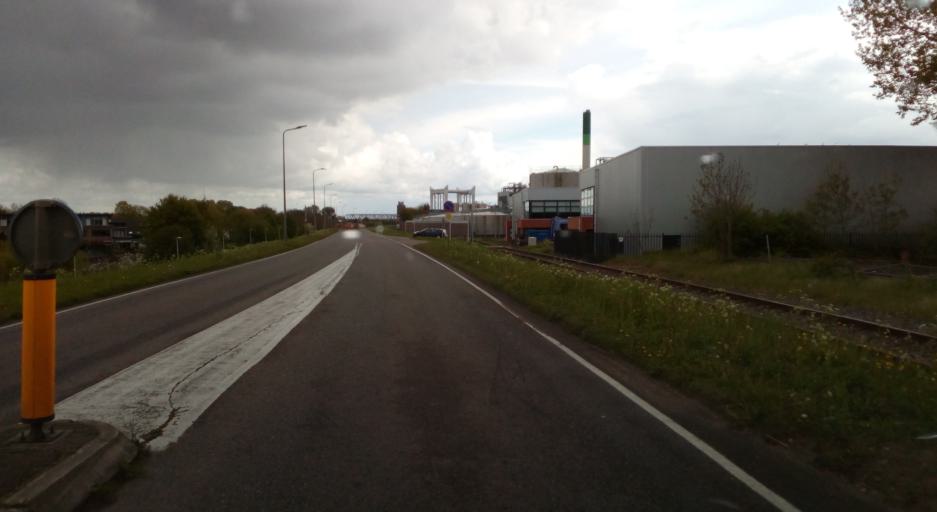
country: NL
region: South Holland
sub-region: Gemeente Zwijndrecht
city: Zwijndrecht
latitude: 51.8058
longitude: 4.6326
